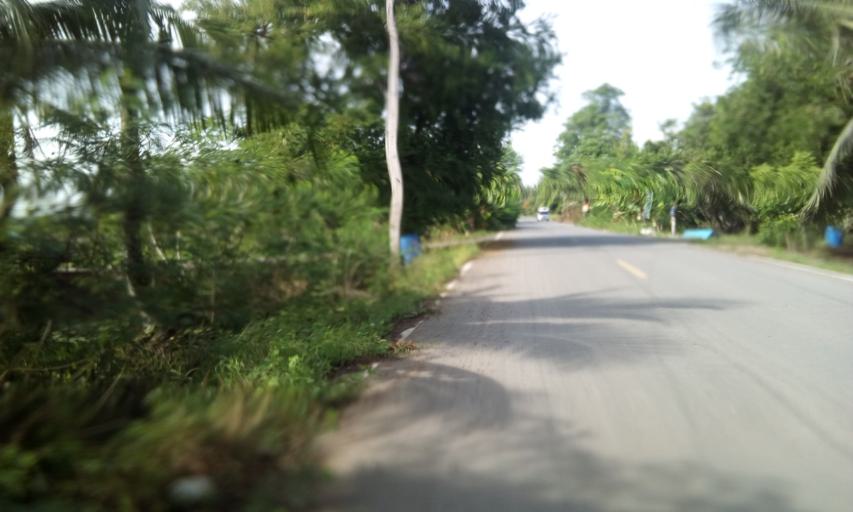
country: TH
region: Pathum Thani
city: Ban Lam Luk Ka
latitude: 14.0183
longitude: 100.8464
